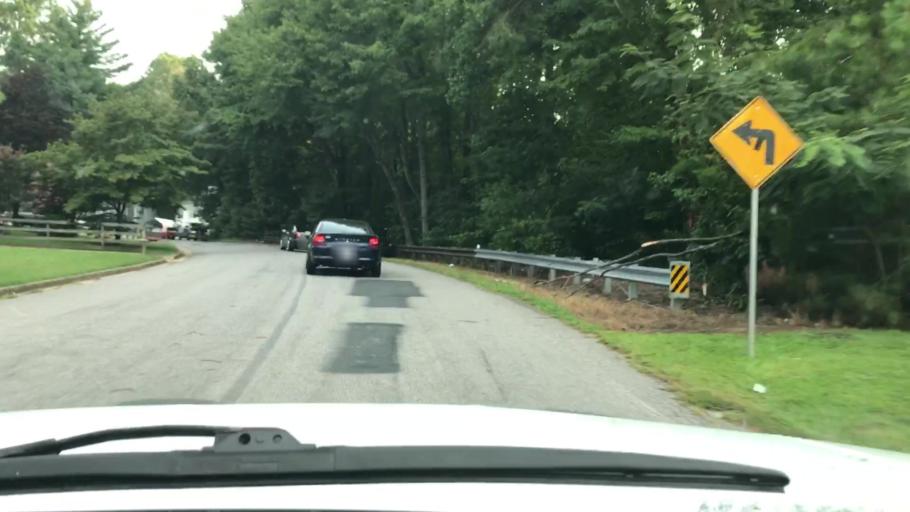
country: US
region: Virginia
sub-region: Chesterfield County
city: Chesterfield
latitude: 37.4432
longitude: -77.5189
